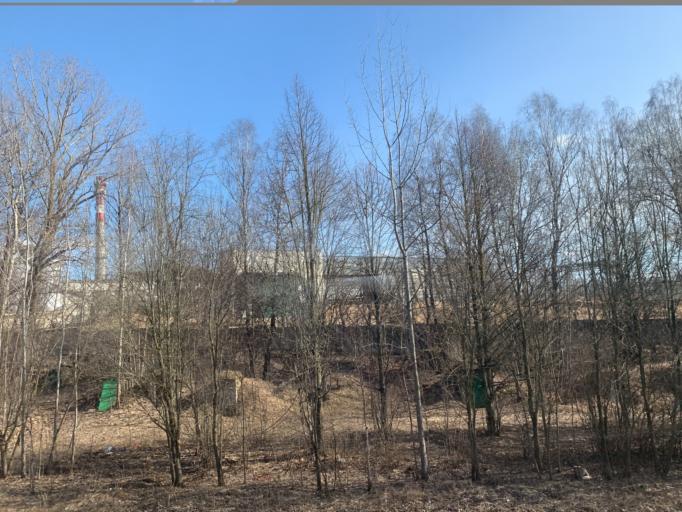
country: BY
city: Fanipol
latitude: 53.7393
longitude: 27.3233
